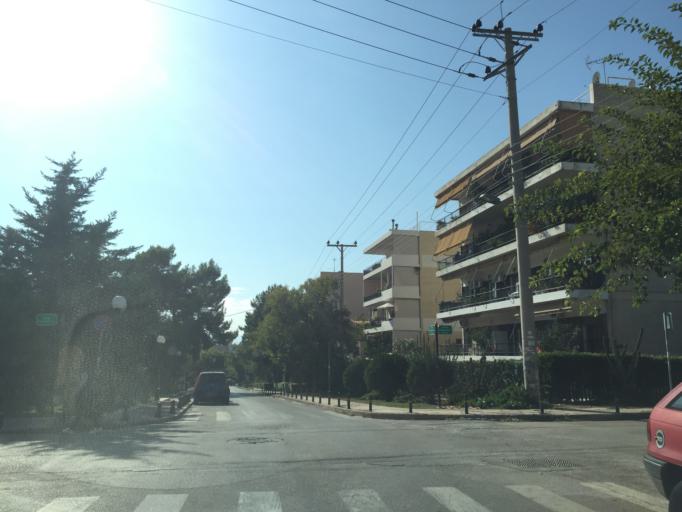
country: GR
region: Attica
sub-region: Nomarchia Anatolikis Attikis
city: Voula
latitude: 37.8469
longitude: 23.7625
